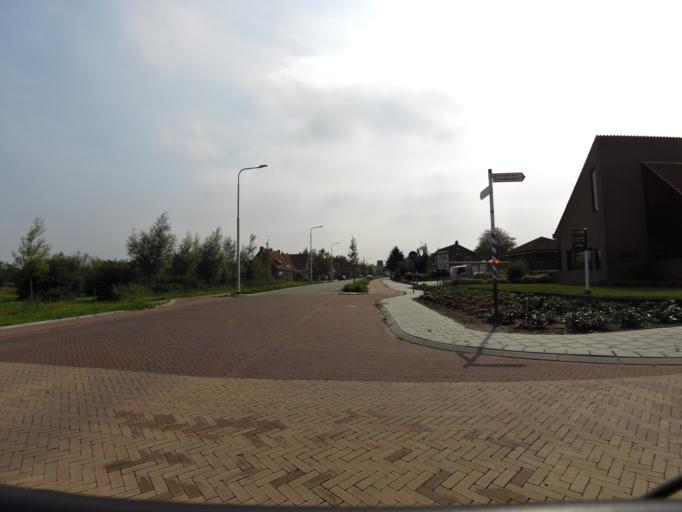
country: NL
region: Zeeland
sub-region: Gemeente Middelburg
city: Middelburg
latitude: 51.5277
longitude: 3.6059
